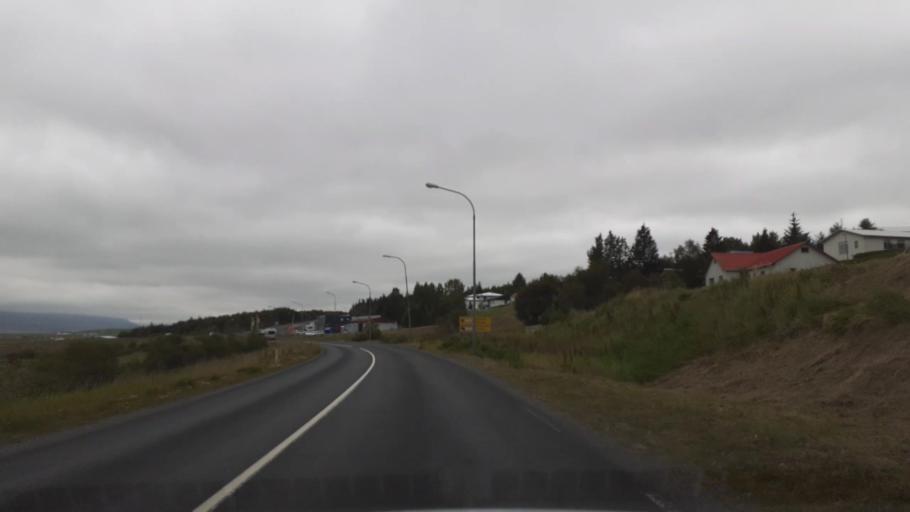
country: IS
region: Northwest
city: Saudarkrokur
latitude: 65.5558
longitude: -19.4500
